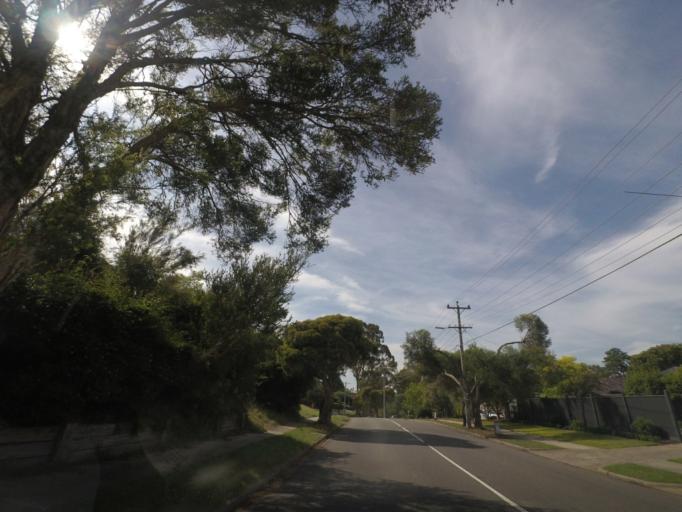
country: AU
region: Victoria
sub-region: Banyule
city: Viewbank
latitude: -37.7415
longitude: 145.0830
